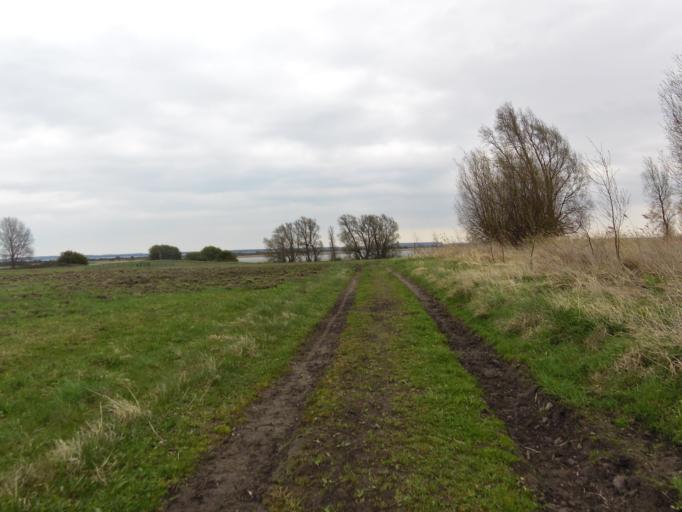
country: DE
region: Mecklenburg-Vorpommern
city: Hiddensee
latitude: 54.5962
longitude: 13.1321
